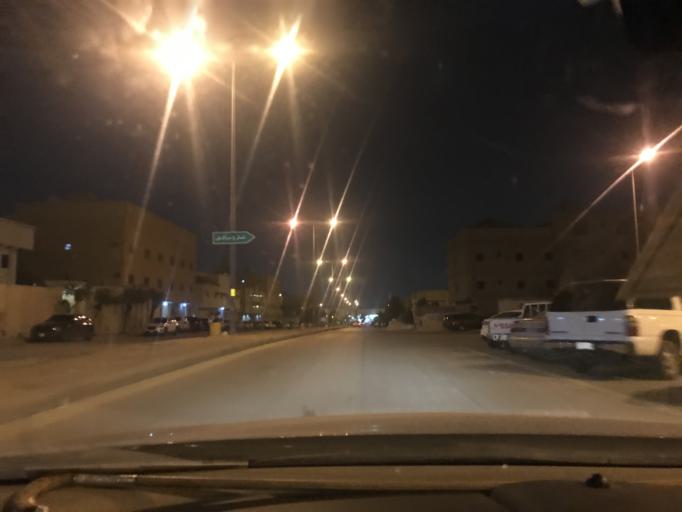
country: SA
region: Ar Riyad
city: Riyadh
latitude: 24.7584
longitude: 46.7470
